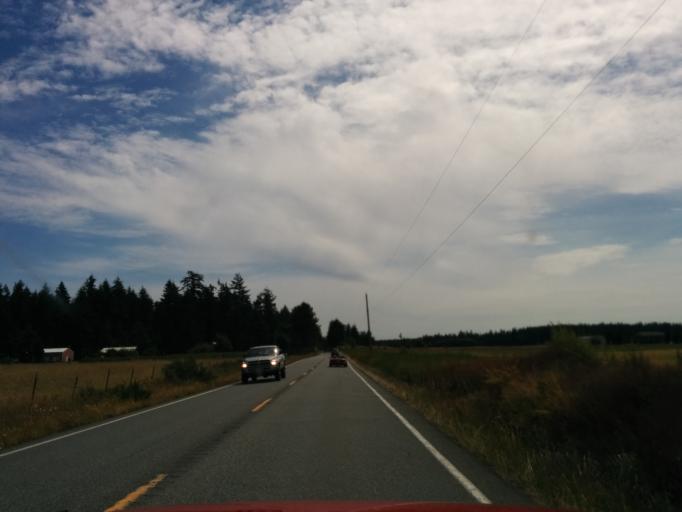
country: US
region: Washington
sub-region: Island County
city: Coupeville
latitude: 48.1936
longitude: -122.6267
